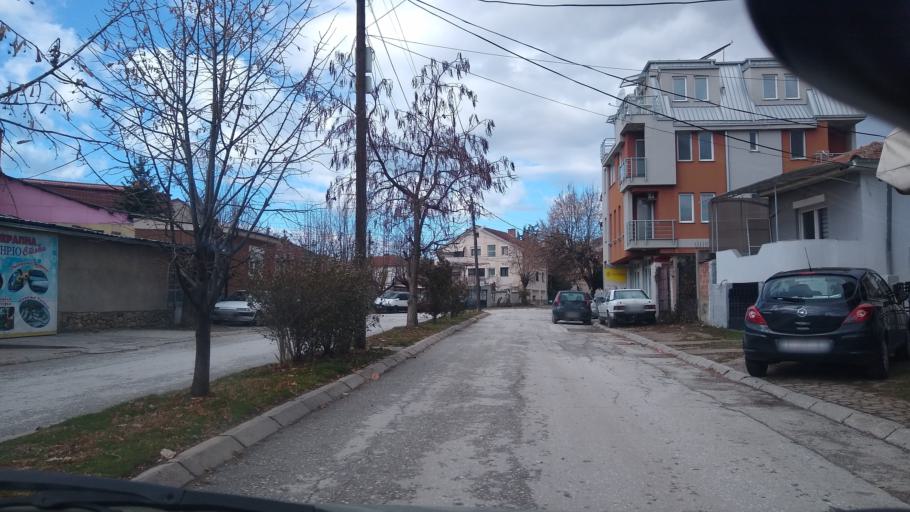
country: MK
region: Bitola
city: Bitola
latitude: 41.0260
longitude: 21.3277
